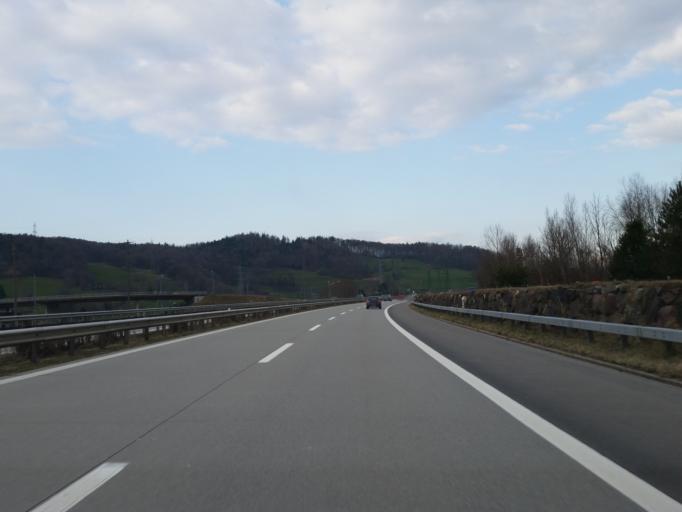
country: CH
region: Saint Gallen
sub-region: Wahlkreis Rheintal
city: Ruthi
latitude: 47.2958
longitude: 9.5528
